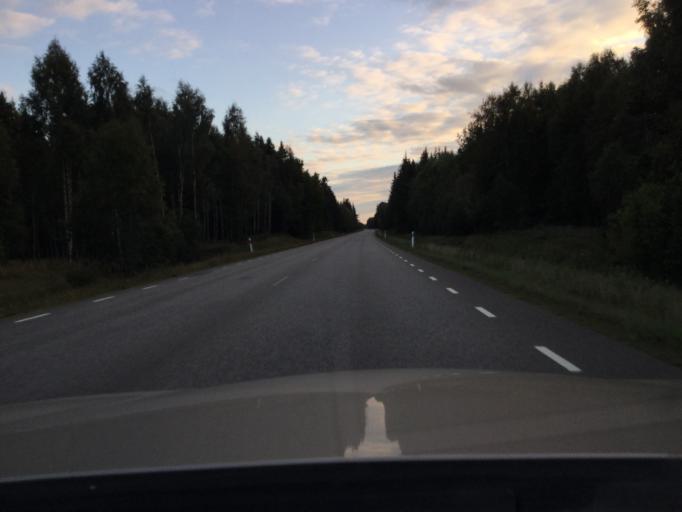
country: SE
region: Kronoberg
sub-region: Almhults Kommun
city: AElmhult
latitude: 56.6082
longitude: 14.2262
